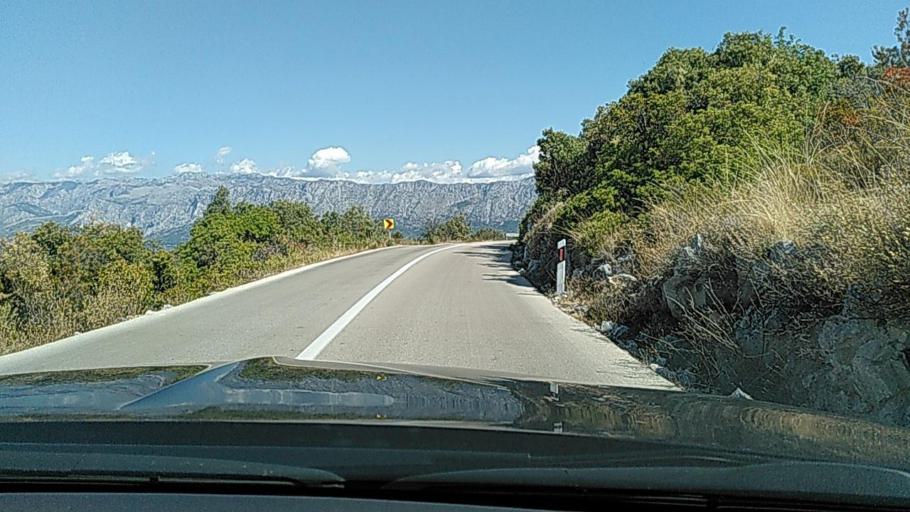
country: HR
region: Dubrovacko-Neretvanska
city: Orebic
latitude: 43.1303
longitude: 17.1249
